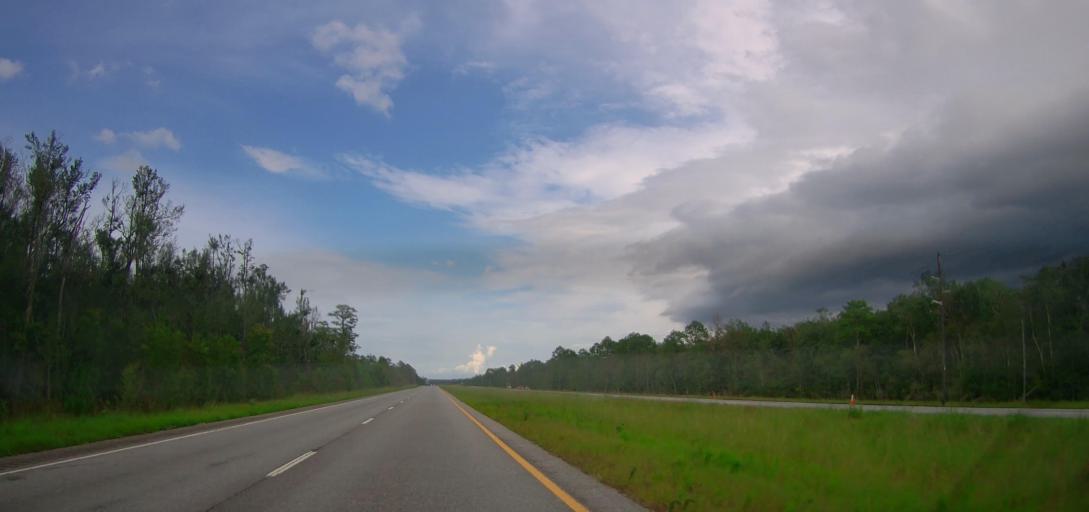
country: US
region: Georgia
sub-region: Pierce County
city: Blackshear
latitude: 31.4370
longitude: -82.0836
